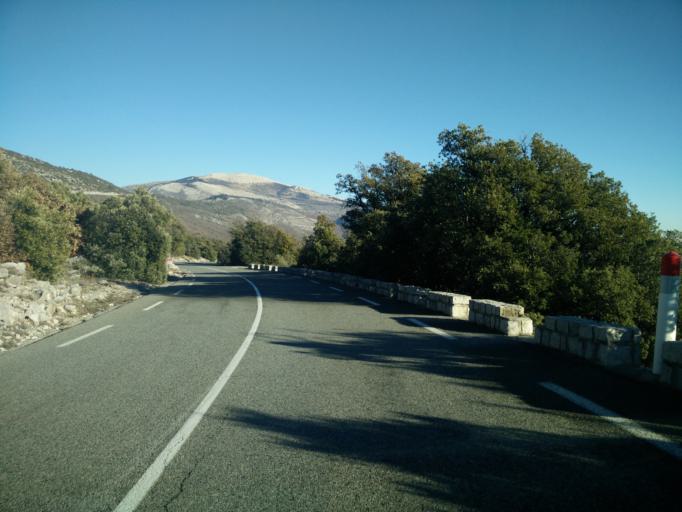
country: FR
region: Provence-Alpes-Cote d'Azur
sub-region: Departement des Alpes-Maritimes
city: Saint-Vallier-de-Thiey
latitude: 43.7030
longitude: 6.8154
